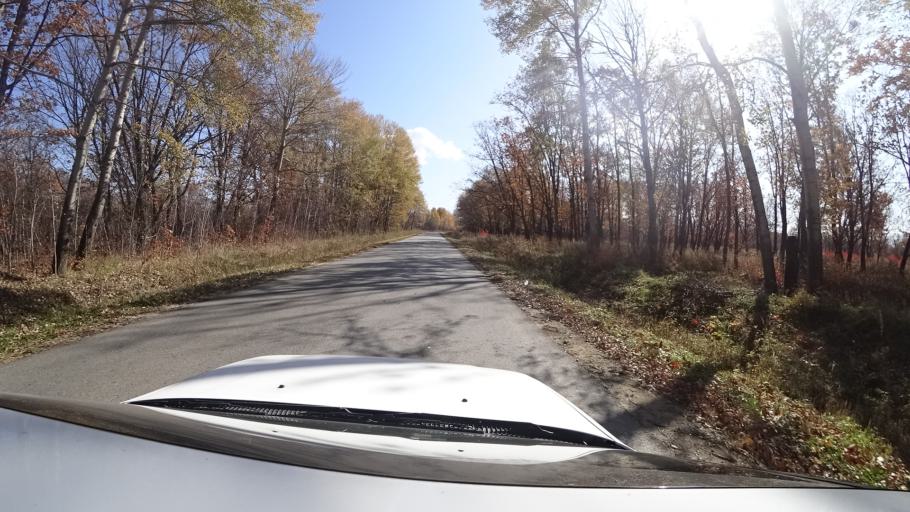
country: RU
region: Primorskiy
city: Lazo
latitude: 45.8712
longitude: 133.6580
